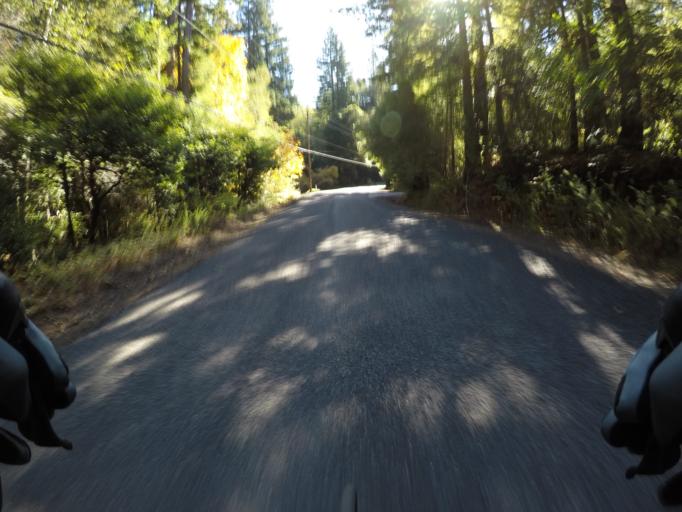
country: US
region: California
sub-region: Santa Cruz County
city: Lompico
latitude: 37.1138
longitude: -122.0207
